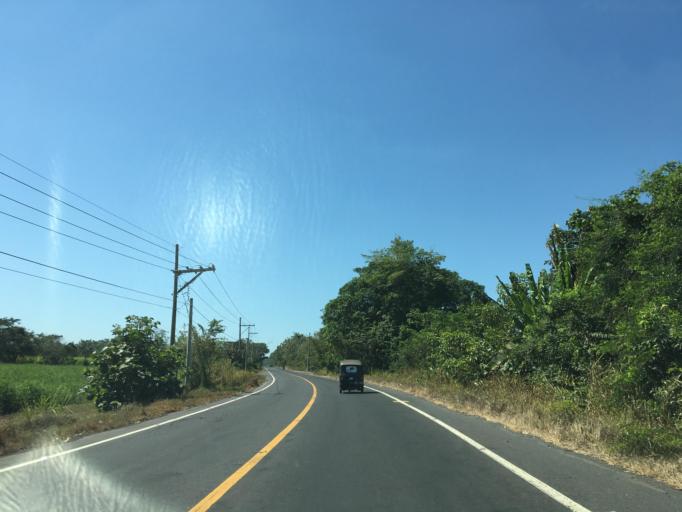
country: GT
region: Escuintla
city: Puerto San Jose
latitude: 14.0200
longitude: -90.8907
